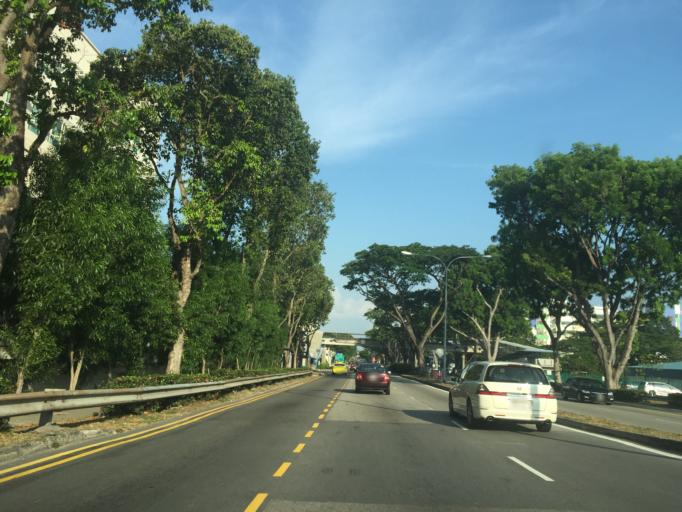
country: SG
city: Singapore
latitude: 1.3409
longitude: 103.9476
